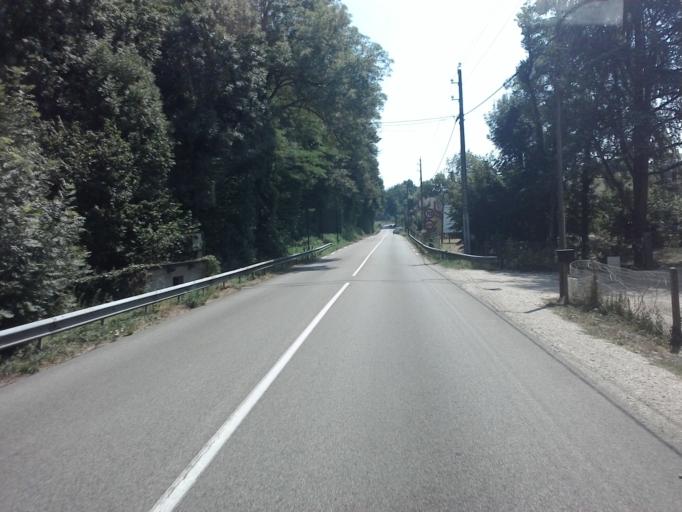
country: FR
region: Rhone-Alpes
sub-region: Departement de l'Isere
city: Corbelin
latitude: 45.6078
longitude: 5.5367
